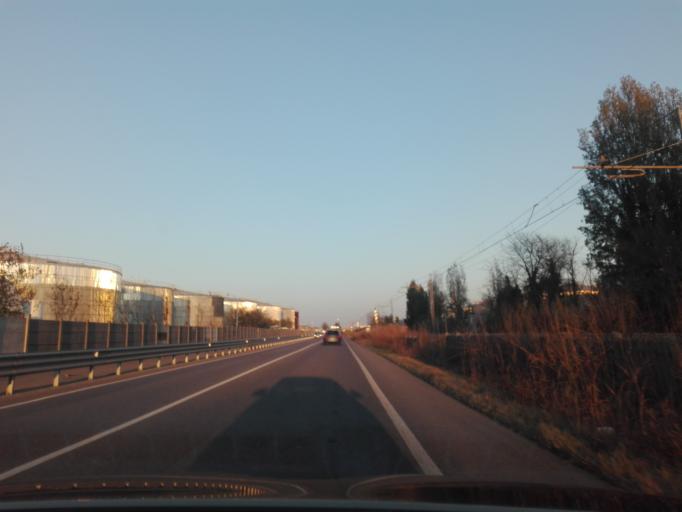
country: IT
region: Lombardy
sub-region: Provincia di Mantova
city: Lunetta-Frassino
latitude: 45.1453
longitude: 10.8184
